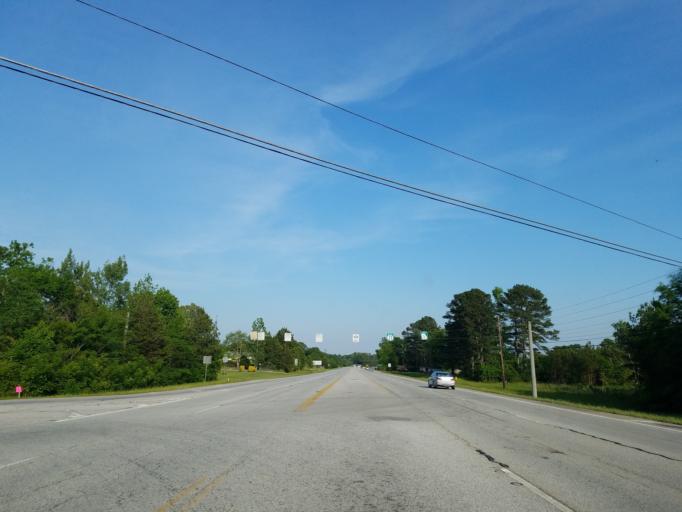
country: US
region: Georgia
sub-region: Floyd County
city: Shannon
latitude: 34.3923
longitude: -85.1898
